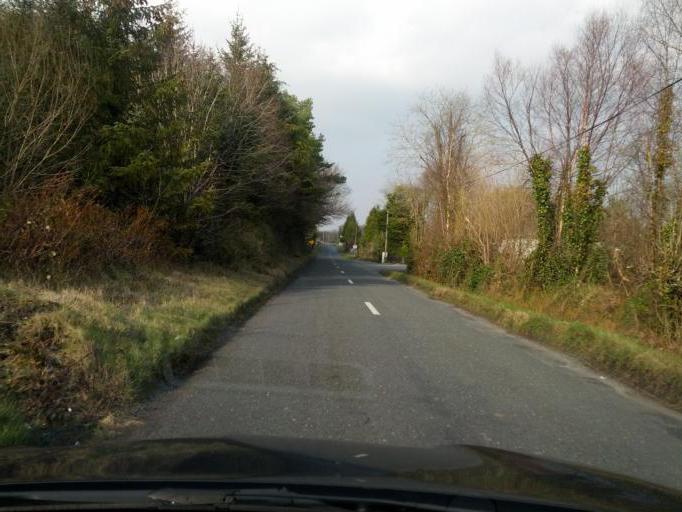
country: IE
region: Connaught
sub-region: County Galway
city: Athenry
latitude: 53.4551
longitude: -8.5502
